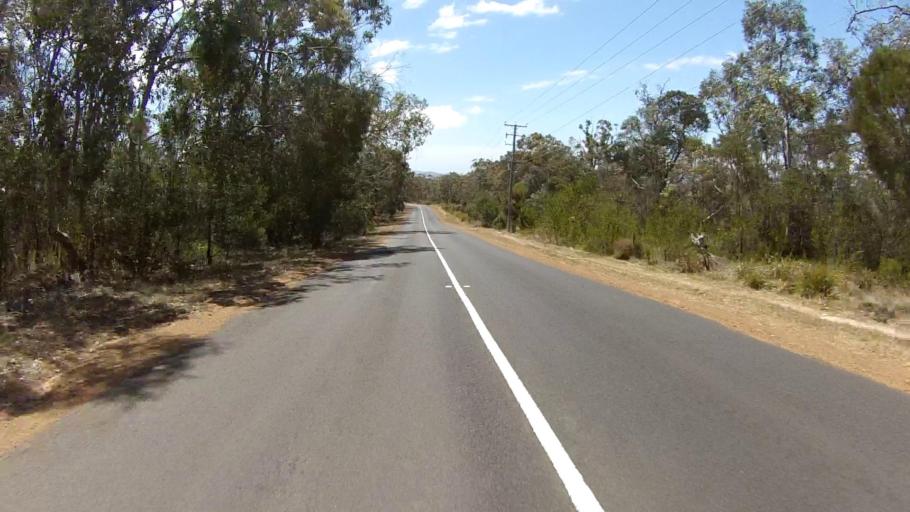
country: AU
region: Tasmania
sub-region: Clarence
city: Sandford
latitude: -43.0103
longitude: 147.4803
